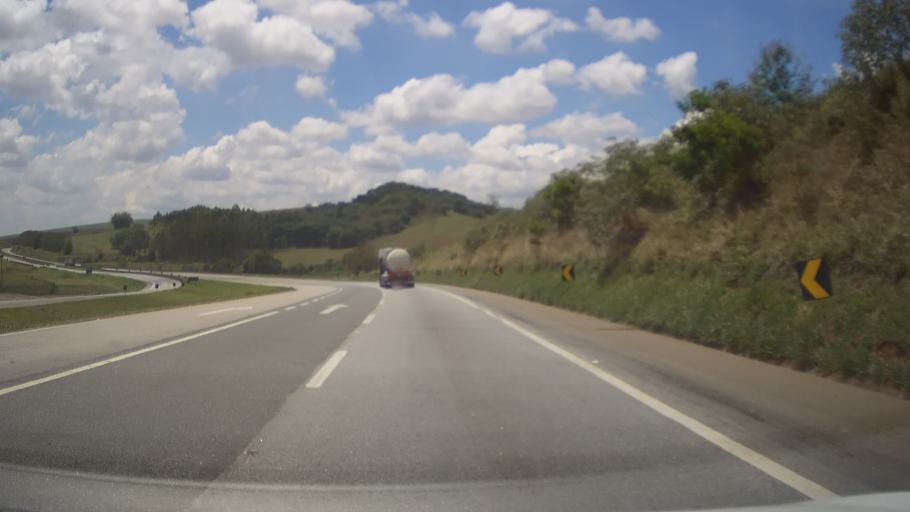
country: BR
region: Minas Gerais
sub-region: Campanha
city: Campanha
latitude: -21.8095
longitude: -45.4850
